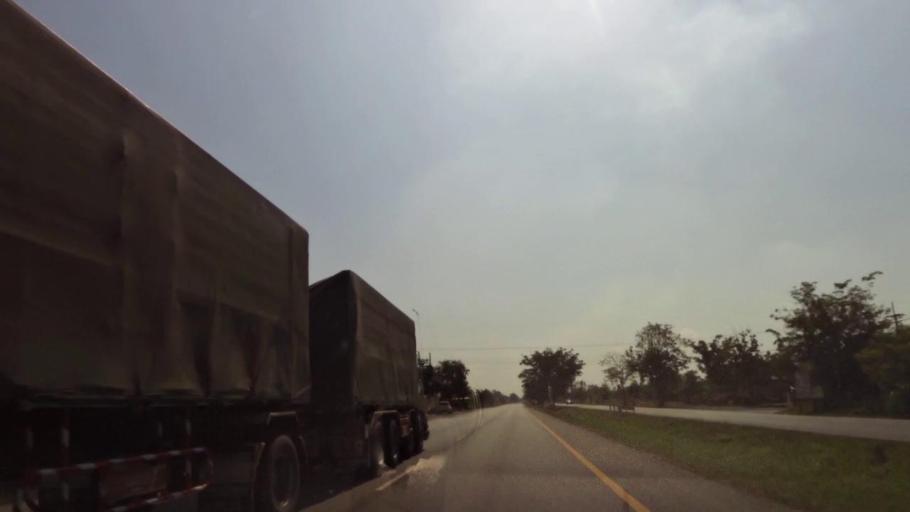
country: TH
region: Phichit
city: Bueng Na Rang
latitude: 16.3088
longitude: 100.1286
